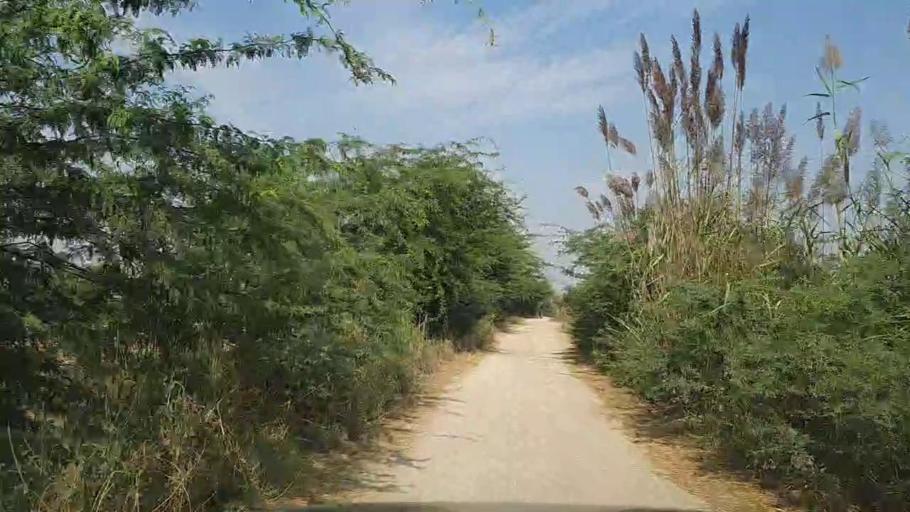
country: PK
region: Sindh
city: Thatta
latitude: 24.7620
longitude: 67.7672
